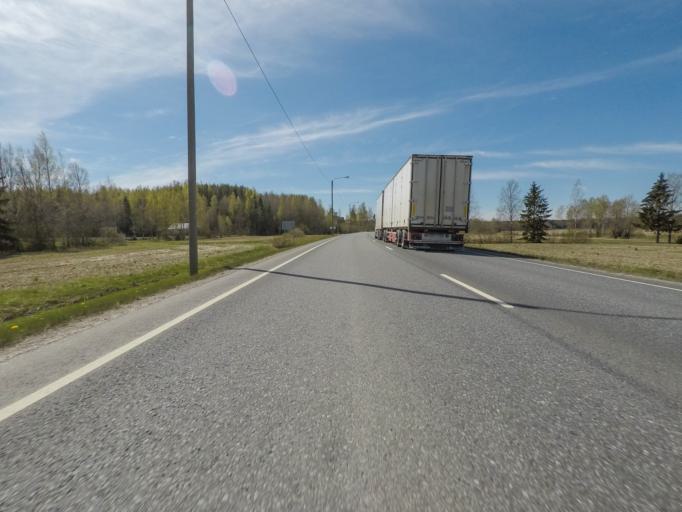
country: FI
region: Pirkanmaa
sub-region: Etelae-Pirkanmaa
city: Urjala
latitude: 61.0219
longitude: 23.4910
